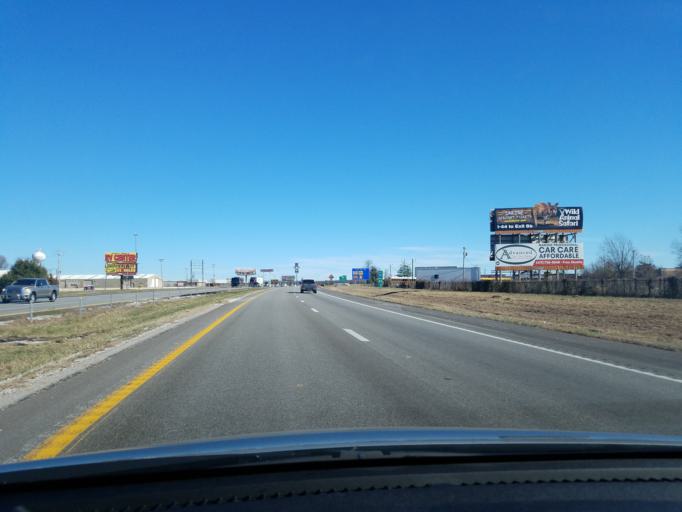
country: US
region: Missouri
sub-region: Greene County
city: Strafford
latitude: 37.2717
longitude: -93.1241
